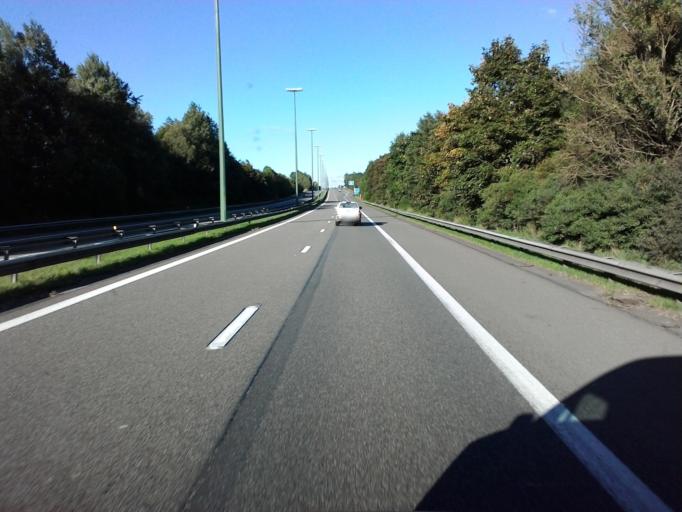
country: BE
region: Wallonia
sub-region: Province du Luxembourg
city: Houffalize
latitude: 50.1359
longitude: 5.7744
